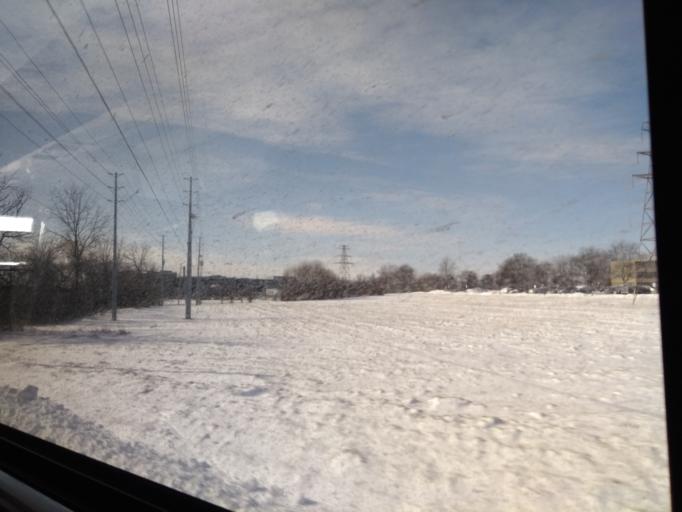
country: CA
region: Ontario
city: Niagara Falls
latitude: 43.1001
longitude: -79.0857
